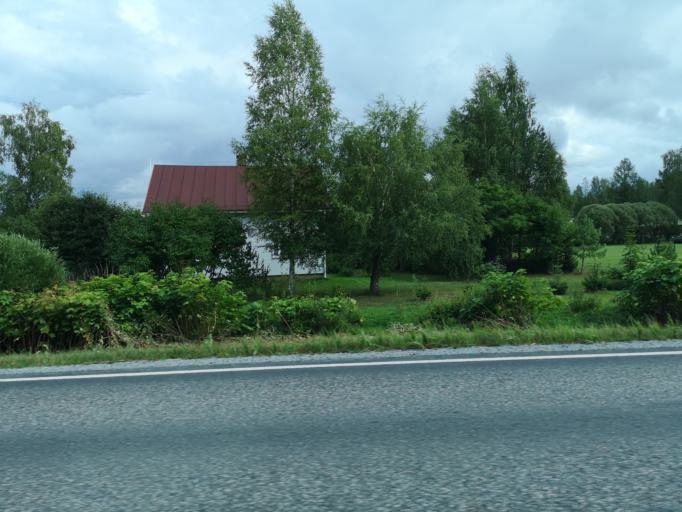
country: FI
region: Central Finland
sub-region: Jyvaeskylae
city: Hankasalmi
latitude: 62.3594
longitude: 26.4522
